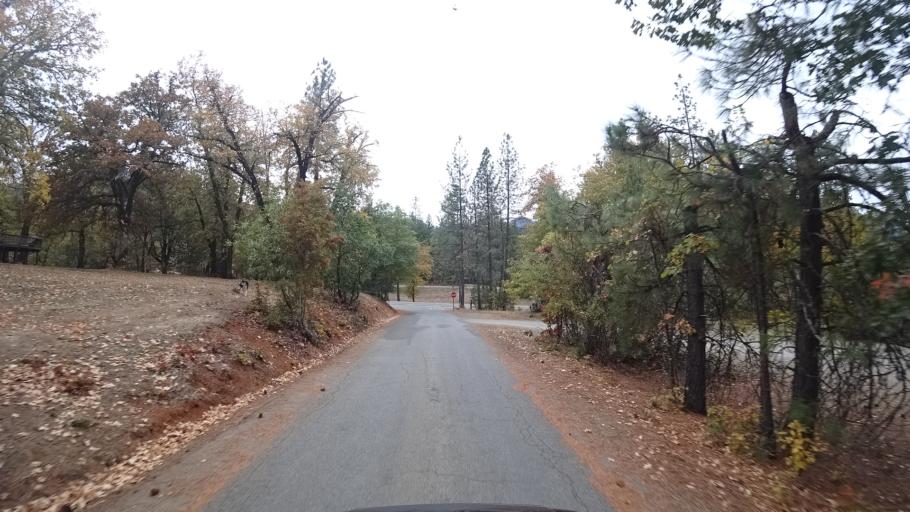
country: US
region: California
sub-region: Siskiyou County
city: Happy Camp
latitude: 41.8385
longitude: -123.1874
